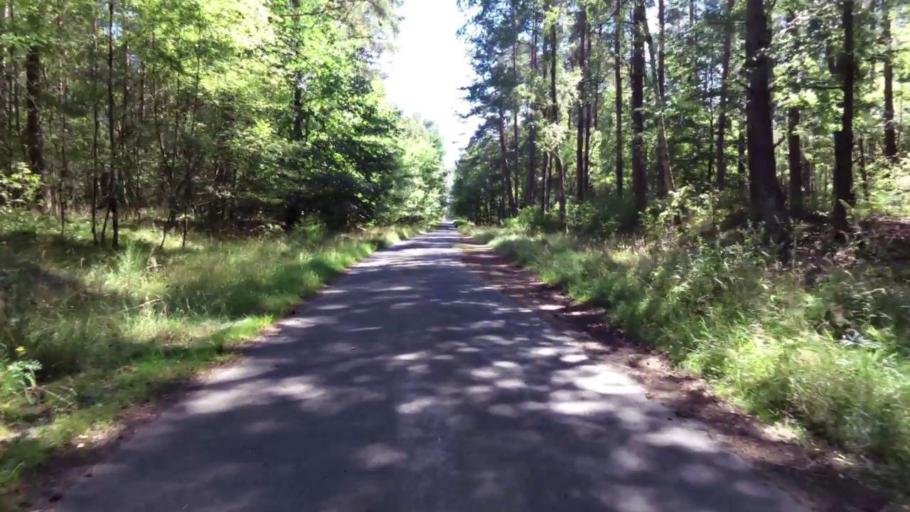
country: PL
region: West Pomeranian Voivodeship
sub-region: Powiat szczecinecki
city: Borne Sulinowo
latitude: 53.5966
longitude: 16.6344
